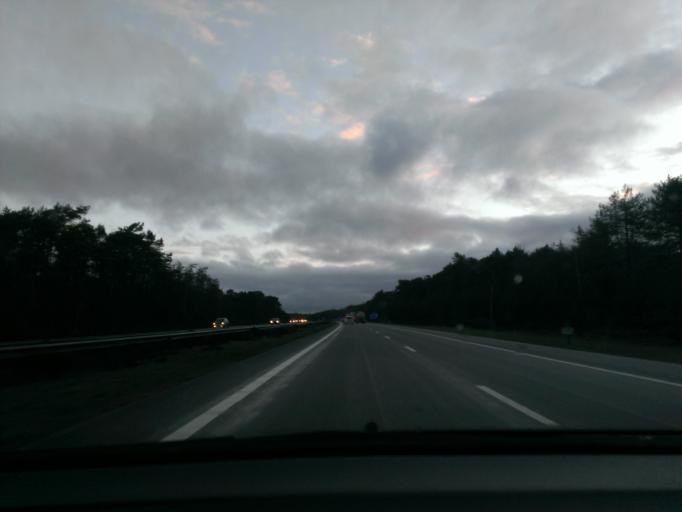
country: NL
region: Gelderland
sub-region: Gemeente Hattem
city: Hattem
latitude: 52.4514
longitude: 6.0292
